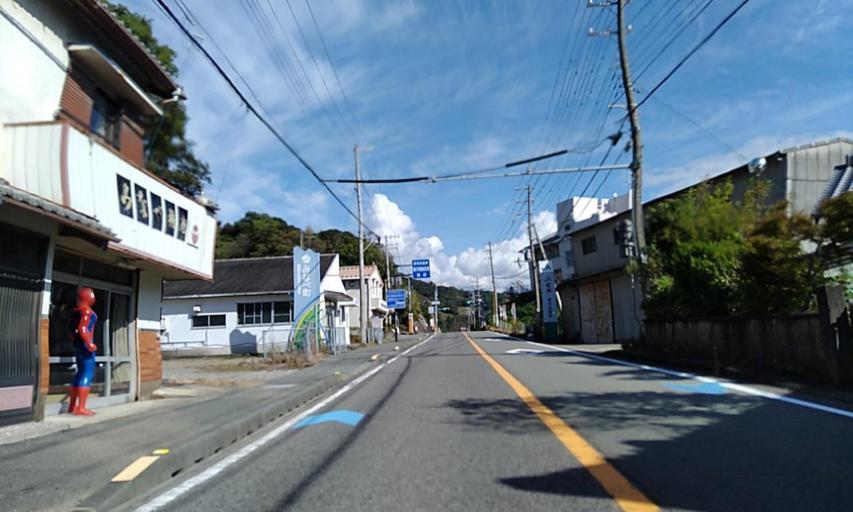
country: JP
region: Wakayama
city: Tanabe
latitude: 33.7819
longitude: 135.2799
